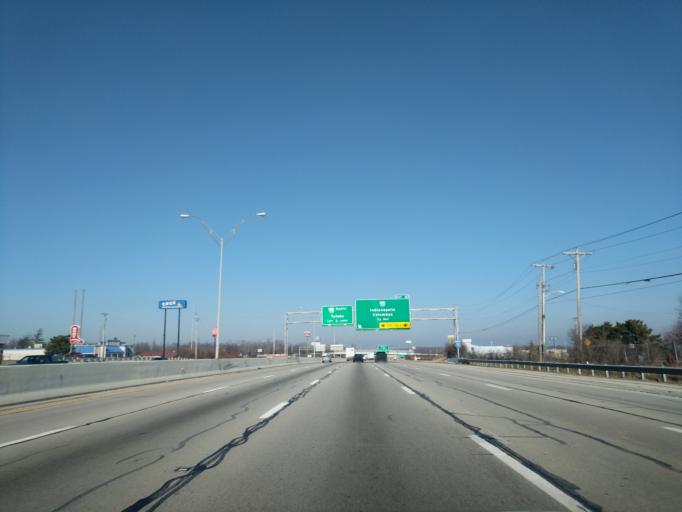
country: US
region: Ohio
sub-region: Montgomery County
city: Vandalia
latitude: 39.8504
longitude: -84.1897
